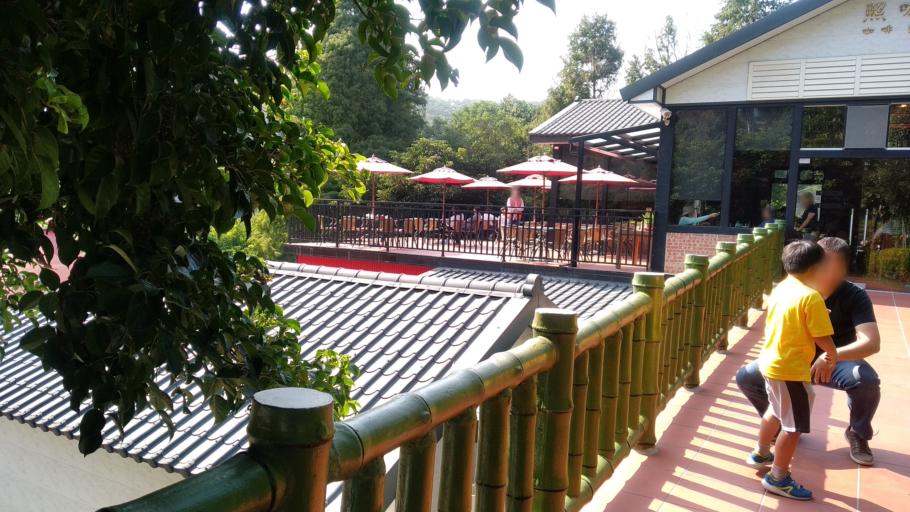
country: TW
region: Taiwan
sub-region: Hsinchu
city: Zhubei
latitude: 24.8625
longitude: 121.1055
